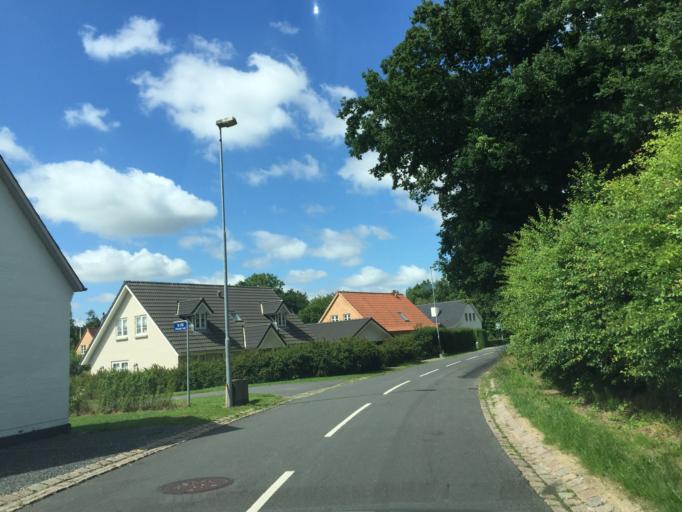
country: DK
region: South Denmark
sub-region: Odense Kommune
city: Neder Holluf
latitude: 55.3584
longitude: 10.4476
